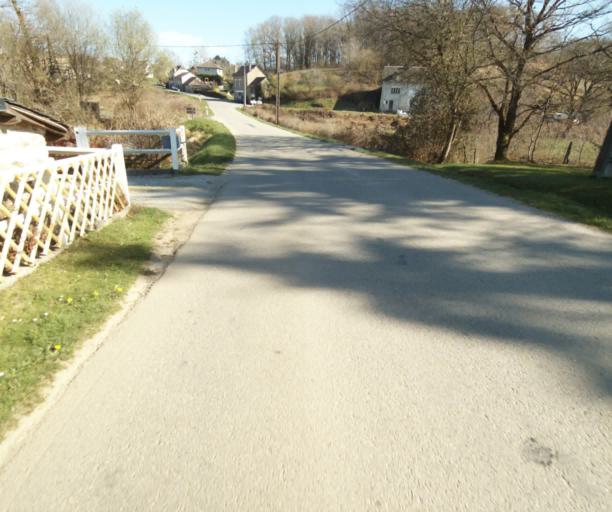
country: FR
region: Limousin
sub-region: Departement de la Correze
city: Chamboulive
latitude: 45.4700
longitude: 1.7226
